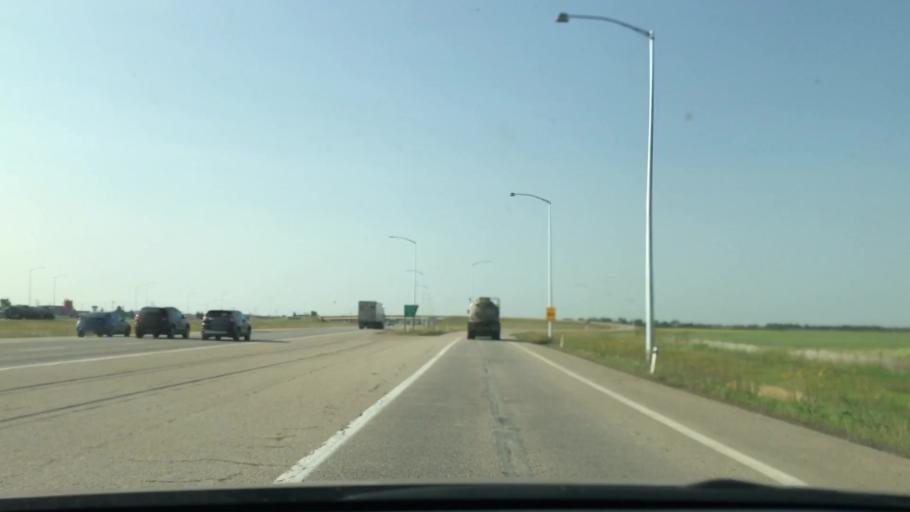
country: CA
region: Alberta
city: Leduc
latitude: 53.2913
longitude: -113.5501
